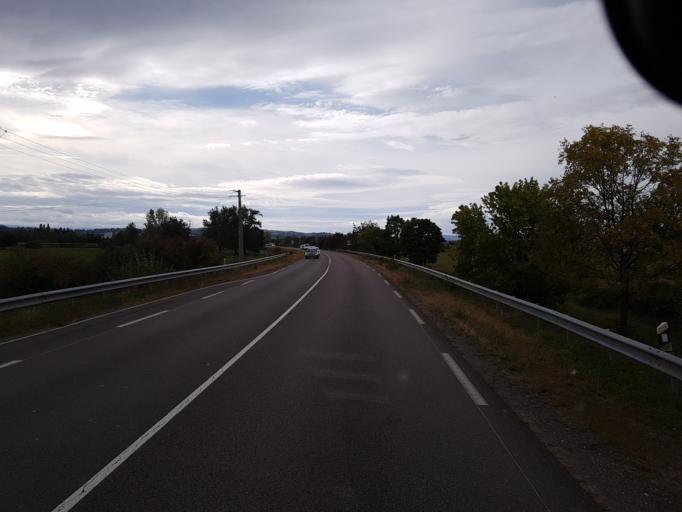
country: FR
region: Rhone-Alpes
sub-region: Departement de la Loire
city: Veauche
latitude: 45.5558
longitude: 4.3065
